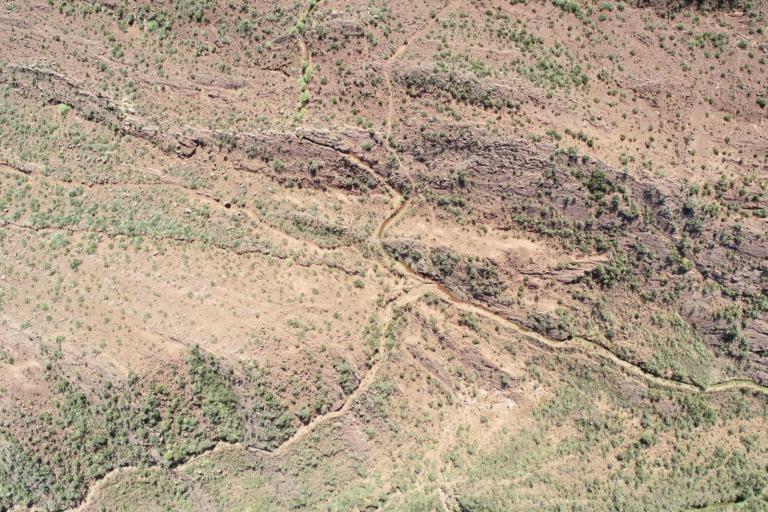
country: BO
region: La Paz
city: Tiahuanaco
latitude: -16.6063
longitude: -68.7583
